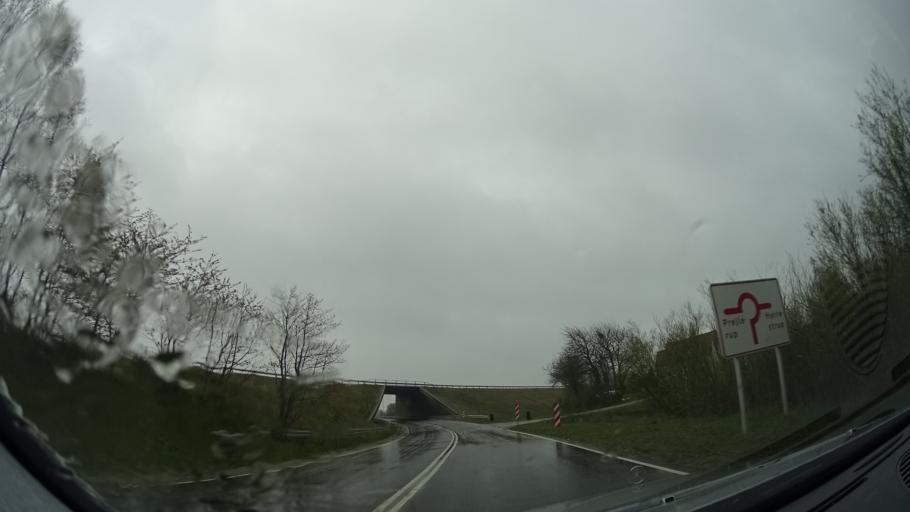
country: DK
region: Zealand
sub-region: Odsherred Kommune
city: Asnaes
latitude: 55.8166
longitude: 11.5824
